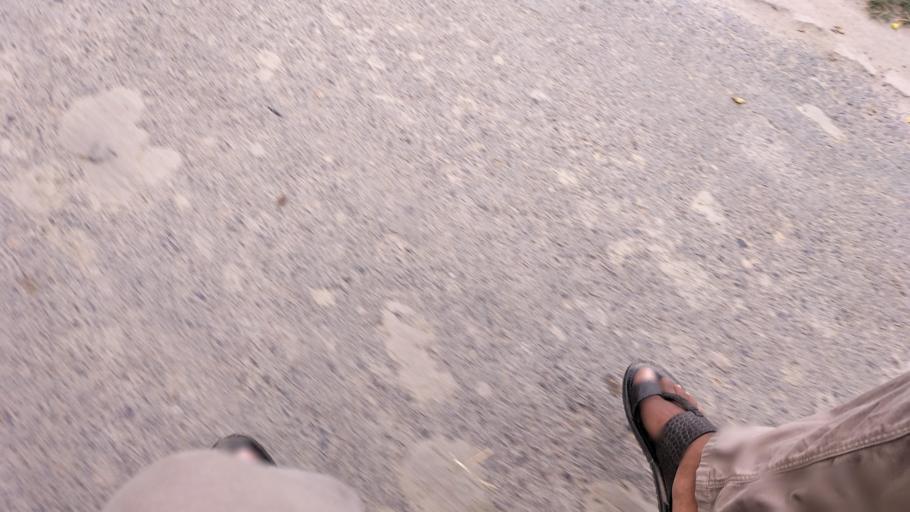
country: BD
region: Rajshahi
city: Rajshahi
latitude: 24.5134
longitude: 88.6350
